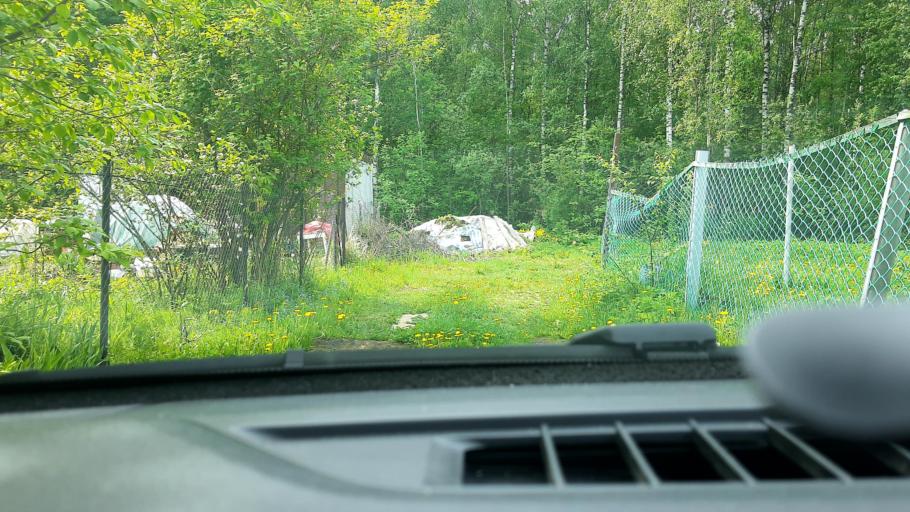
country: RU
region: Nizjnij Novgorod
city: Gorbatovka
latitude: 56.3039
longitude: 43.7654
